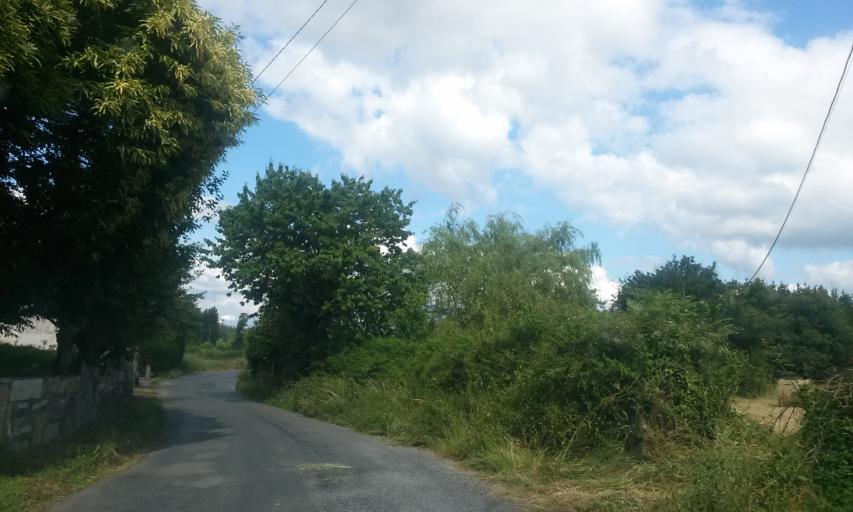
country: ES
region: Galicia
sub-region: Provincia de Lugo
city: Begonte
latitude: 43.1181
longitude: -7.6637
